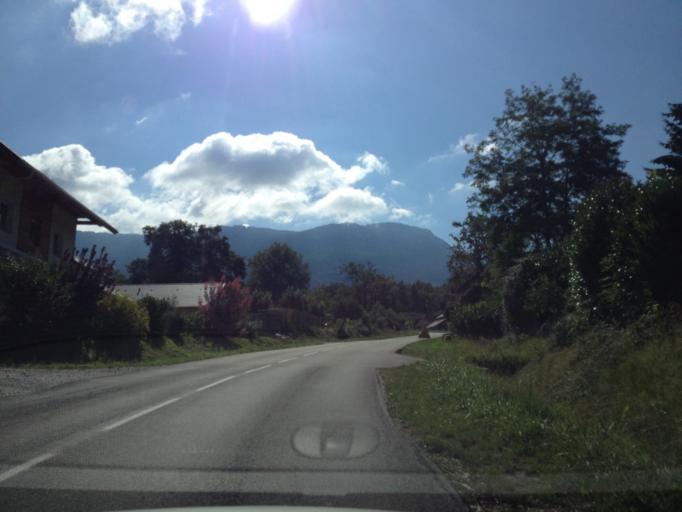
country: FR
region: Rhone-Alpes
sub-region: Departement de la Savoie
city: Gresy-sur-Aix
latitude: 45.7185
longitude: 5.9472
